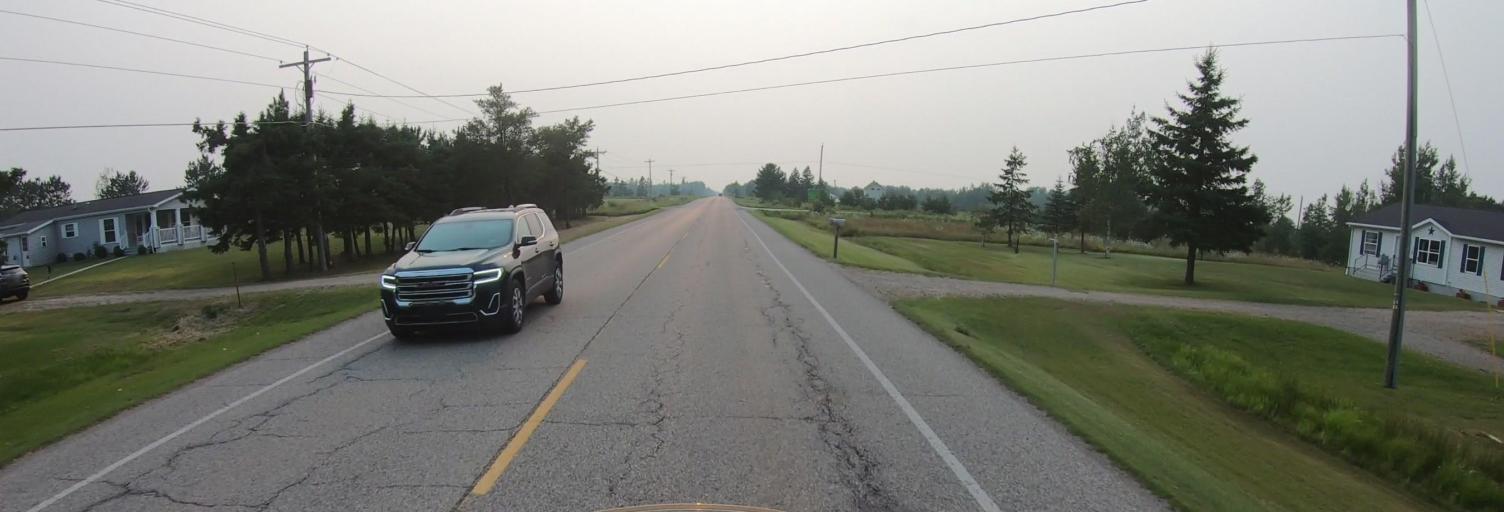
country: US
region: Michigan
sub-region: Chippewa County
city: Sault Ste. Marie
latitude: 46.4191
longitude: -84.4461
